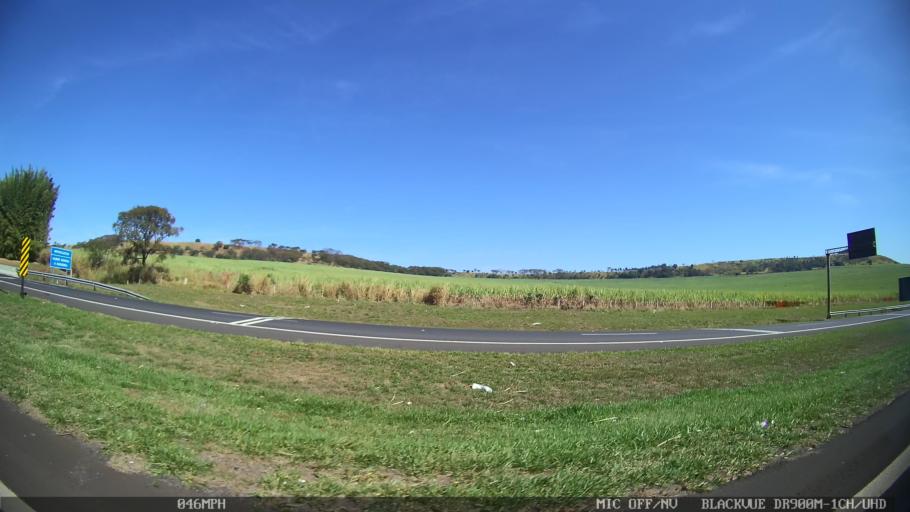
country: BR
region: Sao Paulo
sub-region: Cravinhos
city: Cravinhos
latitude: -21.4114
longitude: -47.6668
